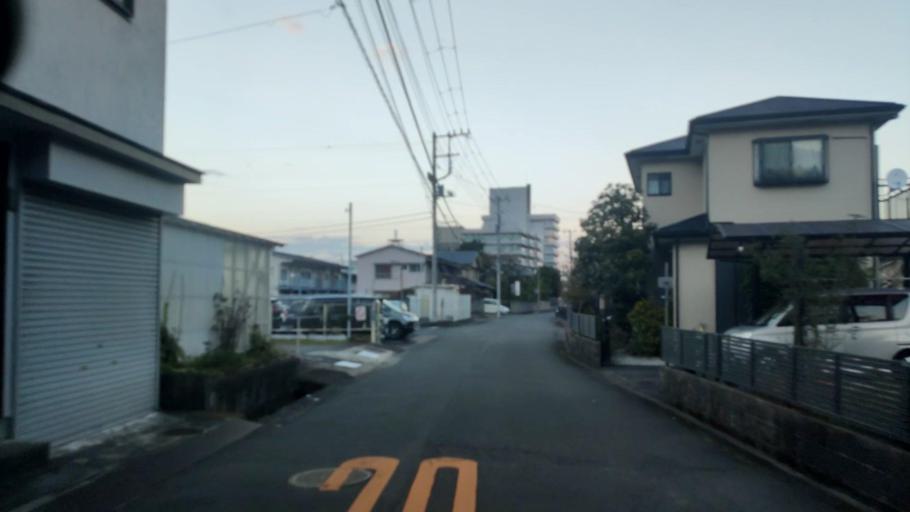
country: JP
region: Shizuoka
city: Ito
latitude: 34.9634
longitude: 139.0928
